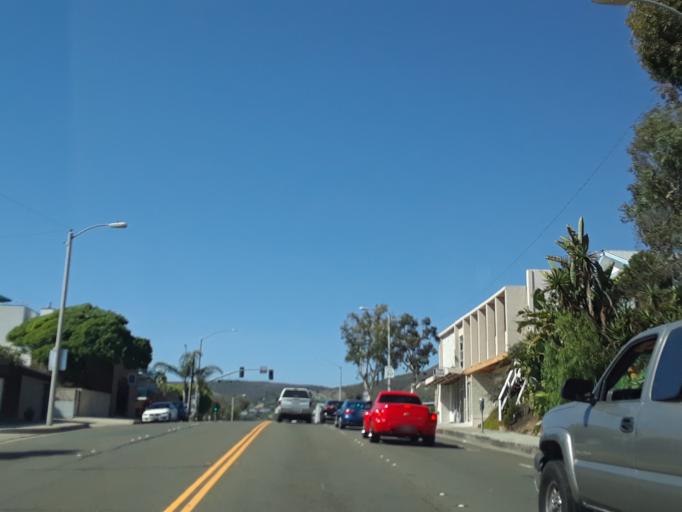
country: US
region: California
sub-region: Orange County
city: Laguna Beach
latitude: 33.5390
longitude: -117.7806
